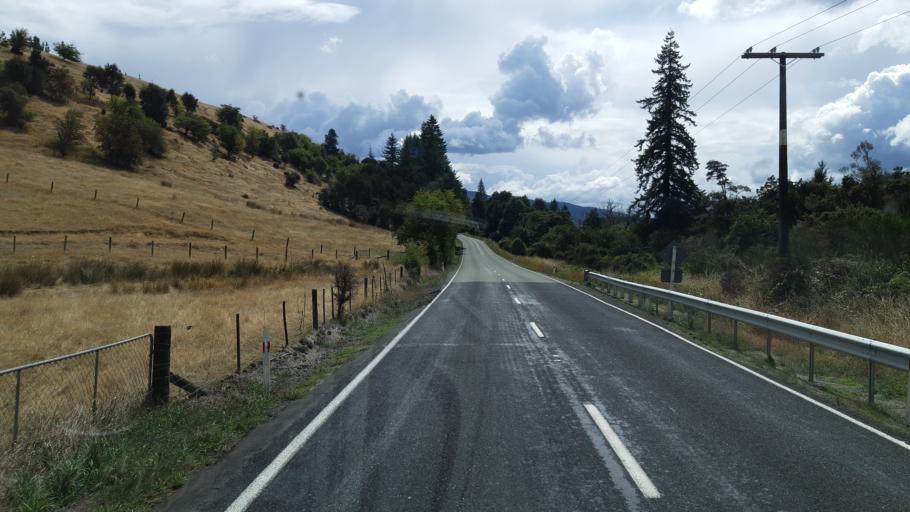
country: NZ
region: Tasman
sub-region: Tasman District
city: Wakefield
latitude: -41.5036
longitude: 172.7949
